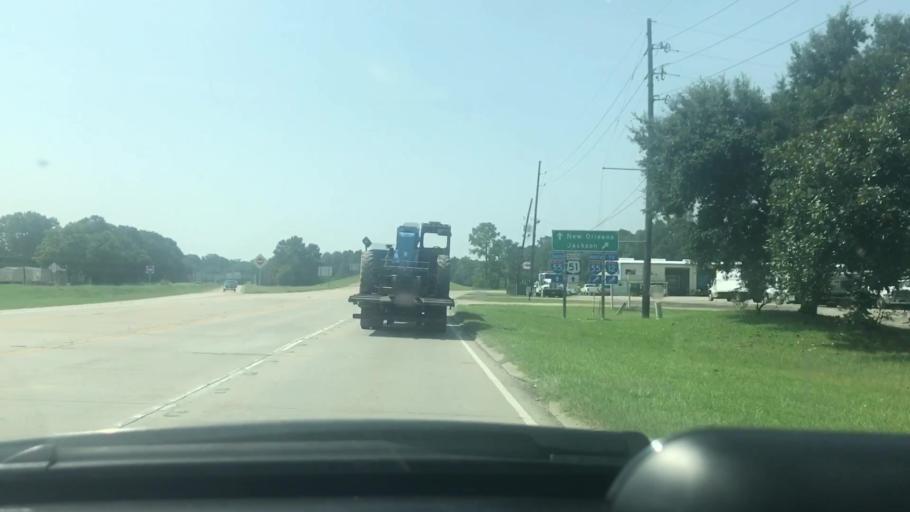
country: US
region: Louisiana
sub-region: Tangipahoa Parish
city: Hammond
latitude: 30.4734
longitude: -90.4827
